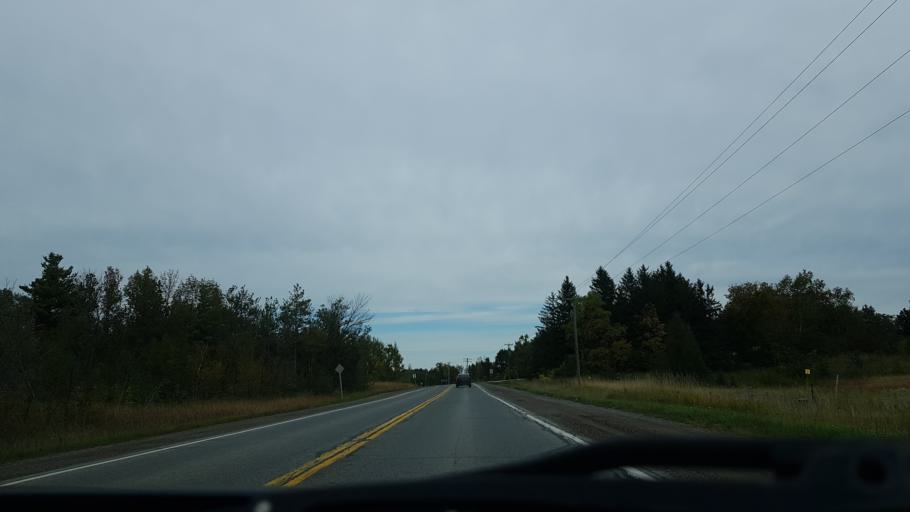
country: CA
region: Ontario
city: Orangeville
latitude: 43.9115
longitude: -79.9378
